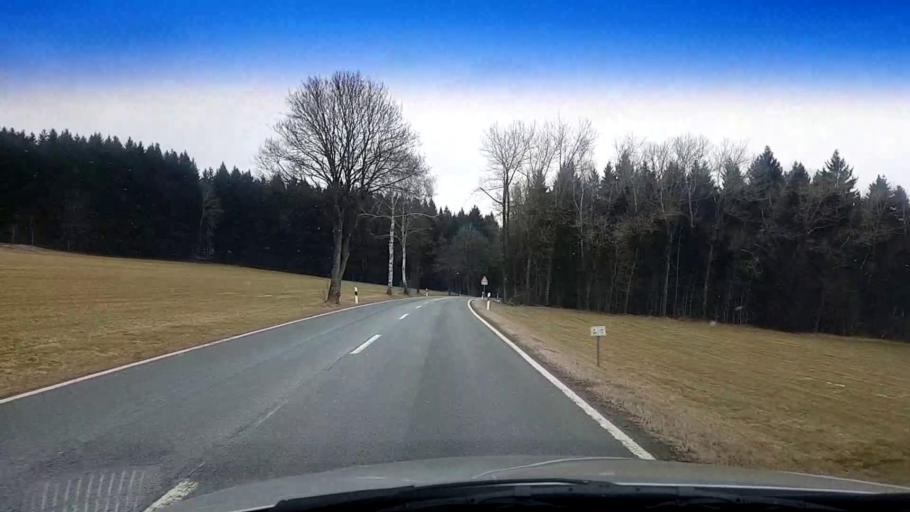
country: DE
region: Bavaria
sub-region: Upper Franconia
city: Marktleugast
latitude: 50.1734
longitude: 11.6514
